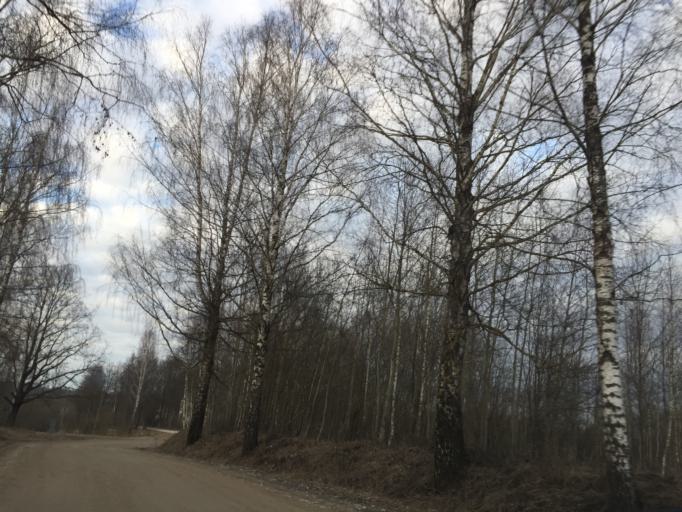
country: LV
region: Jaunjelgava
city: Jaunjelgava
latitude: 56.6100
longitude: 25.0709
